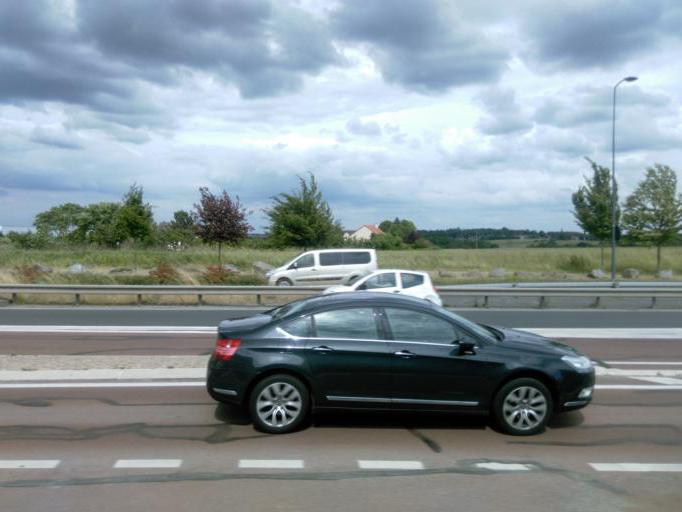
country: FR
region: Ile-de-France
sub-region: Departement du Val-d'Oise
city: Osny
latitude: 49.0723
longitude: 2.0802
